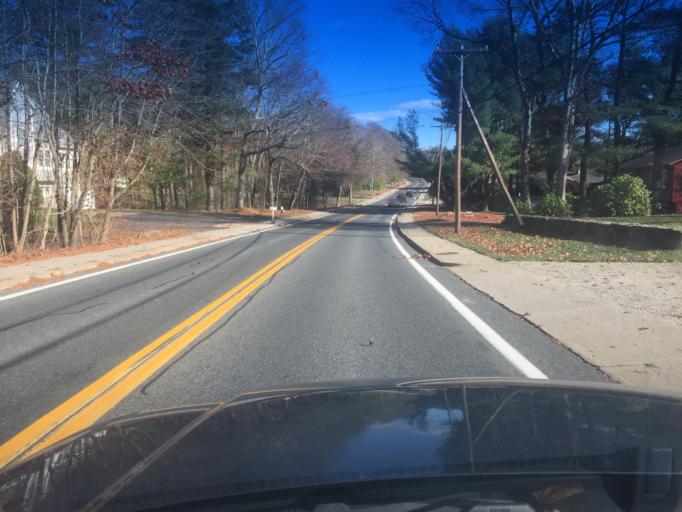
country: US
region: Rhode Island
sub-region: Providence County
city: Greenville
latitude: 41.8646
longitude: -71.5707
